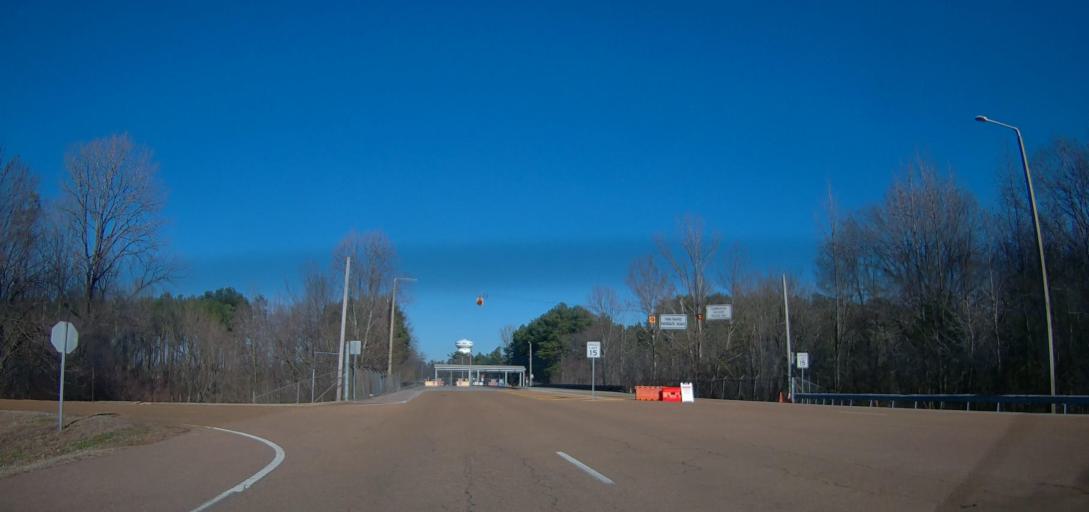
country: US
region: Tennessee
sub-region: Shelby County
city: Millington
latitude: 35.3223
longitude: -89.8706
